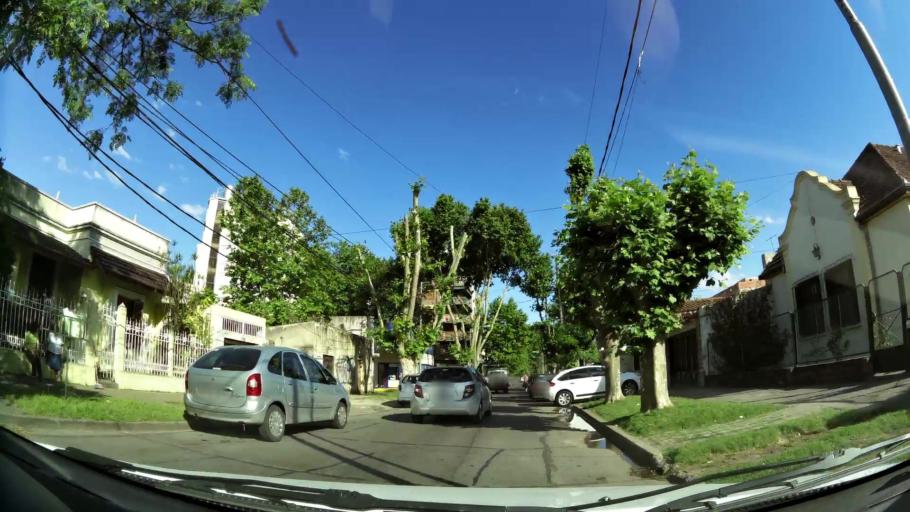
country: AR
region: Buenos Aires
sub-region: Partido de General San Martin
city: General San Martin
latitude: -34.5456
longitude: -58.5501
